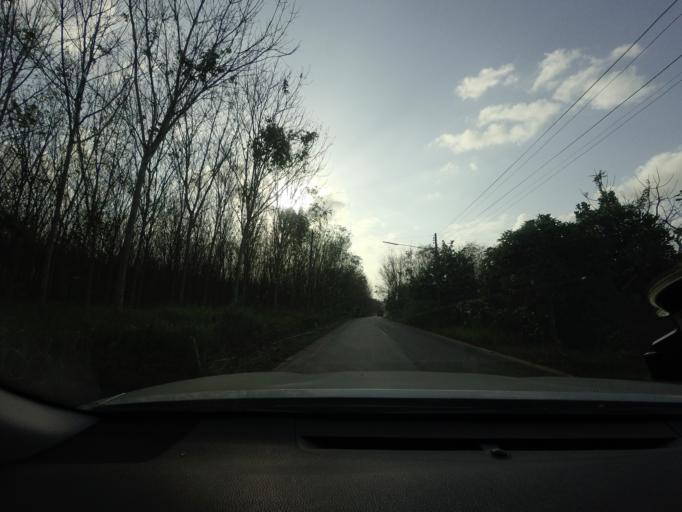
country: TH
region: Pattani
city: Mae Lan
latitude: 6.6155
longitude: 101.2430
